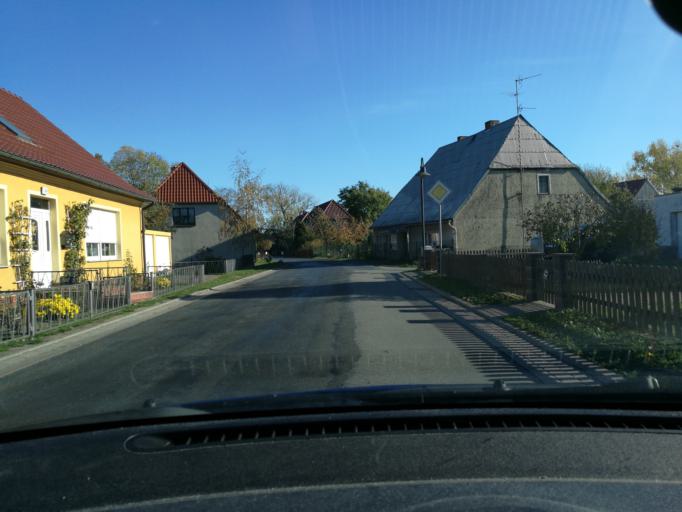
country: DE
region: Brandenburg
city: Lenzen
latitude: 53.1087
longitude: 11.4217
